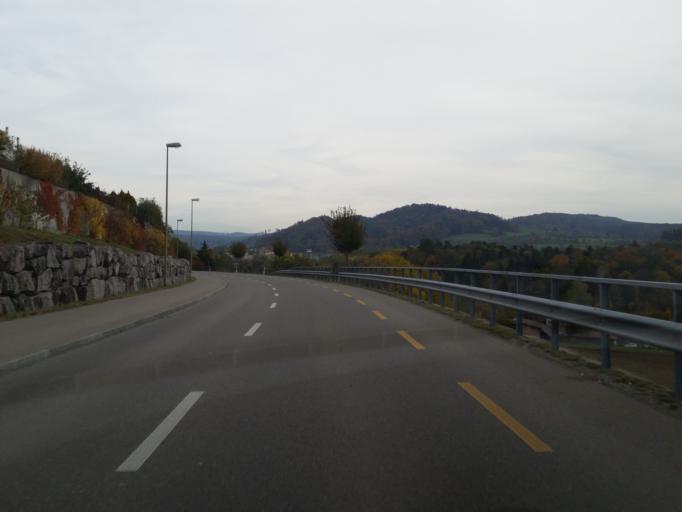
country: CH
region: Zurich
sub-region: Bezirk Winterthur
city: Neftenbach / Dorf Neftenbach
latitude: 47.5206
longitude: 8.6714
